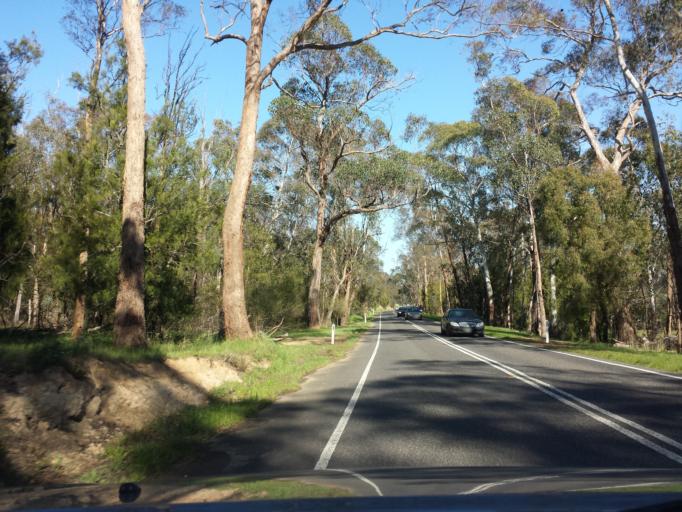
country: AU
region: Victoria
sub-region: Yarra Ranges
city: Yarra Glen
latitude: -37.6485
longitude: 145.3290
